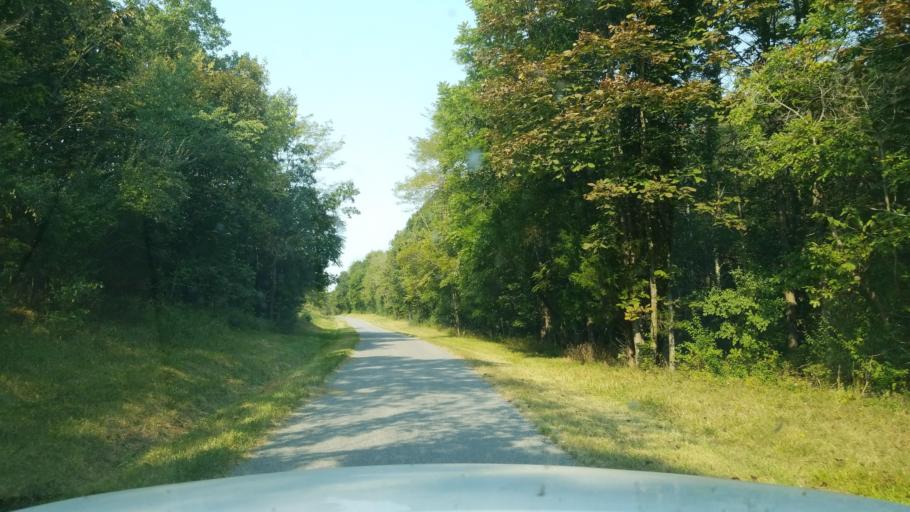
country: US
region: Illinois
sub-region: Saline County
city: Carrier Mills
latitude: 37.7890
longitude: -88.7072
